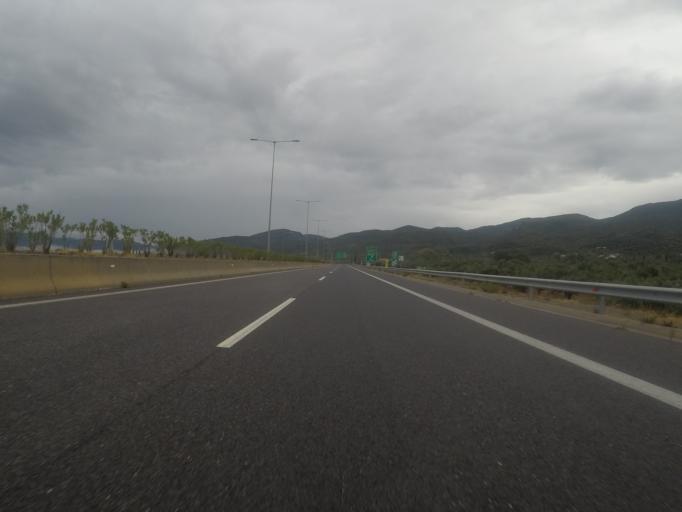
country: GR
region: Peloponnese
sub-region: Nomos Messinias
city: Meligalas
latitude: 37.2416
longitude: 22.0188
